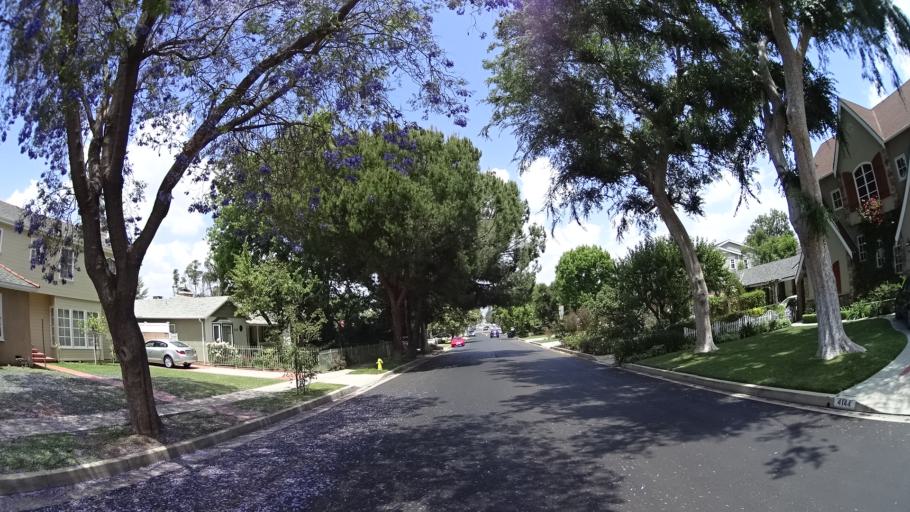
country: US
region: California
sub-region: Los Angeles County
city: Sherman Oaks
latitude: 34.1449
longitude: -118.4225
